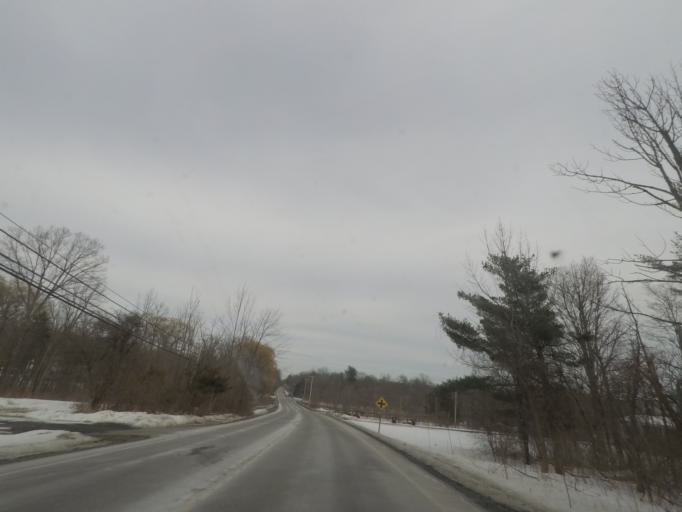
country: US
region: New York
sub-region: Albany County
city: Voorheesville
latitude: 42.5739
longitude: -73.9456
